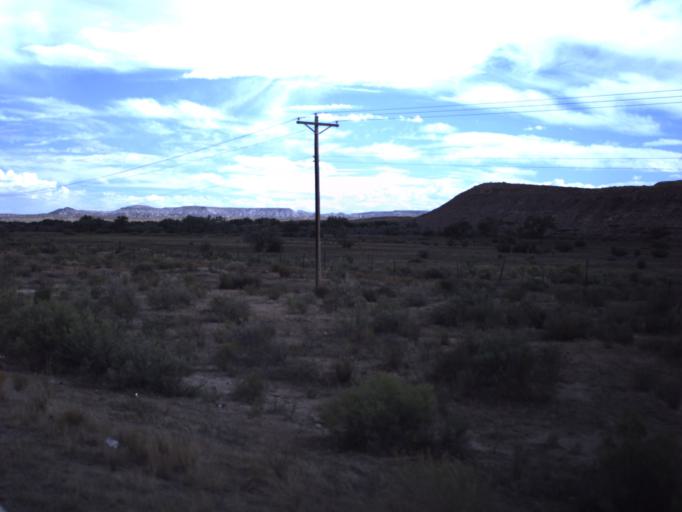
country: US
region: Utah
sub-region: San Juan County
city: Blanding
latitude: 37.2701
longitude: -109.3229
